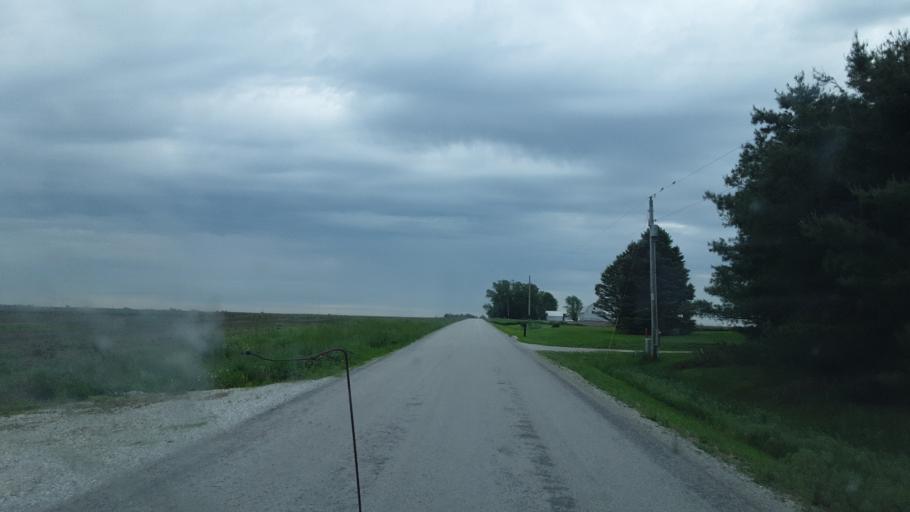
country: US
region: Illinois
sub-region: McDonough County
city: Bushnell
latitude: 40.3809
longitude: -90.5180
